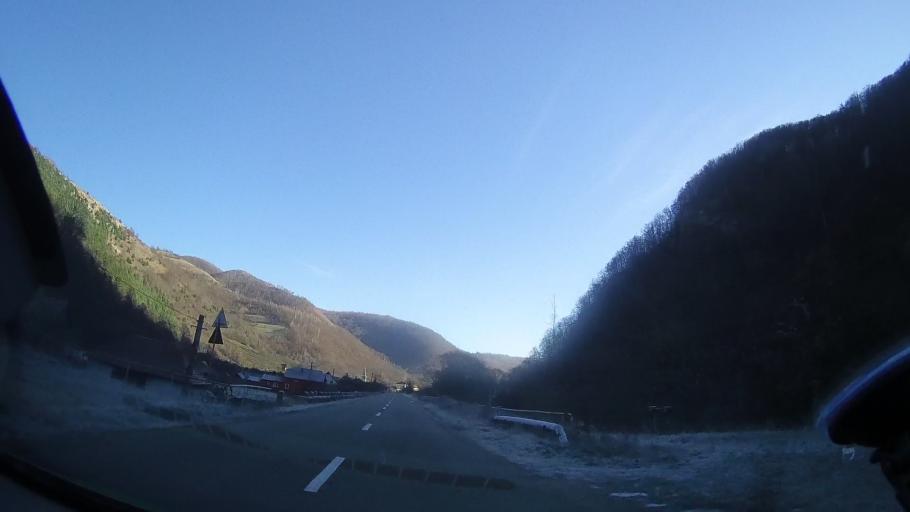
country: RO
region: Bihor
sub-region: Comuna Bulz
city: Bulz
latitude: 46.9146
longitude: 22.6672
